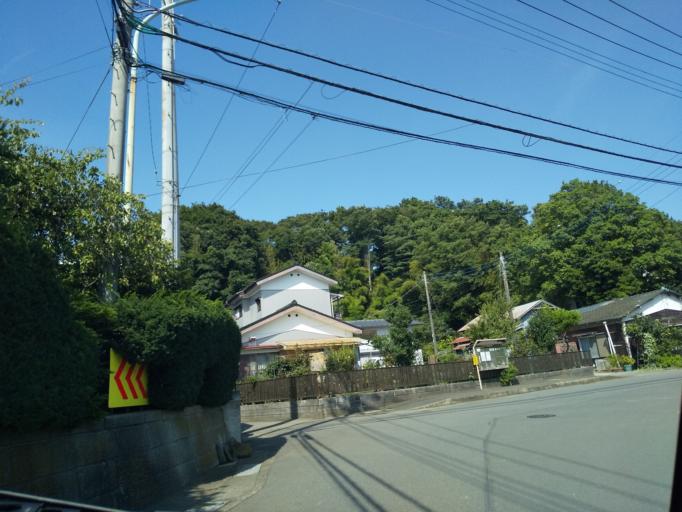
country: JP
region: Kanagawa
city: Zama
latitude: 35.4700
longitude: 139.4135
